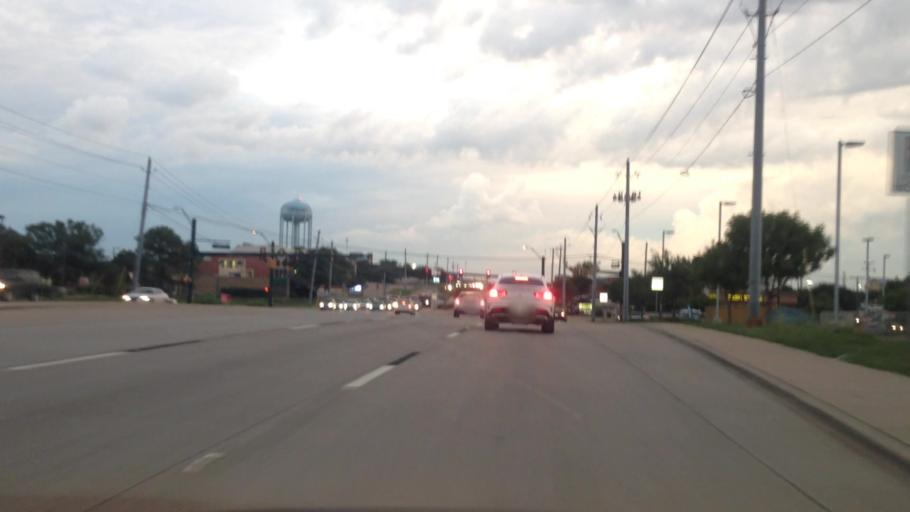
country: US
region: Texas
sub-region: Tarrant County
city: Hurst
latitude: 32.8441
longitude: -97.1863
